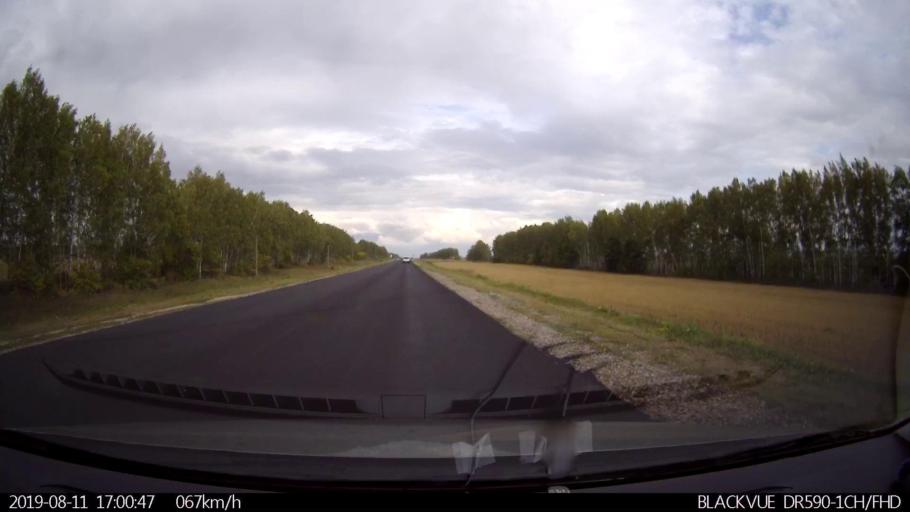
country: RU
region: Ulyanovsk
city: Mayna
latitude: 54.3094
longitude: 47.6851
